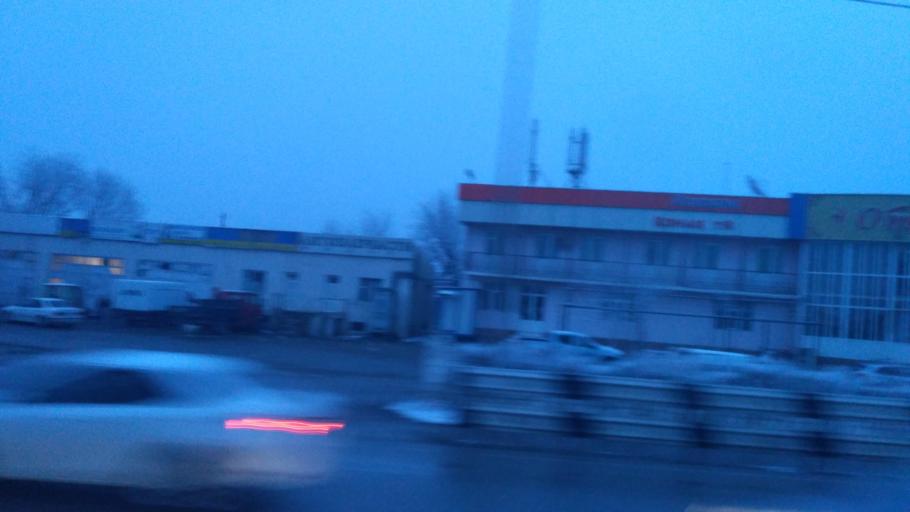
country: KZ
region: Ongtustik Qazaqstan
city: Shymkent
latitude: 42.3623
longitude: 69.5198
